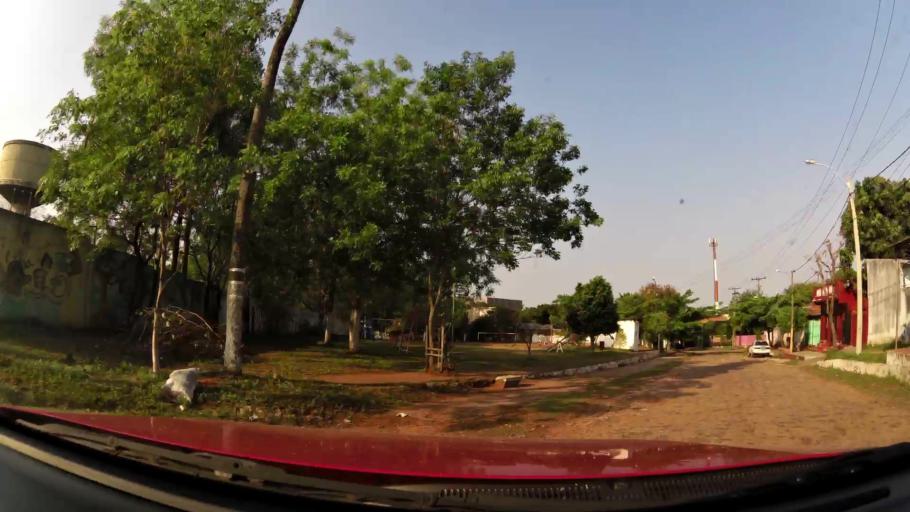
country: PY
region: Central
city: Lambare
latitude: -25.3450
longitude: -57.5936
